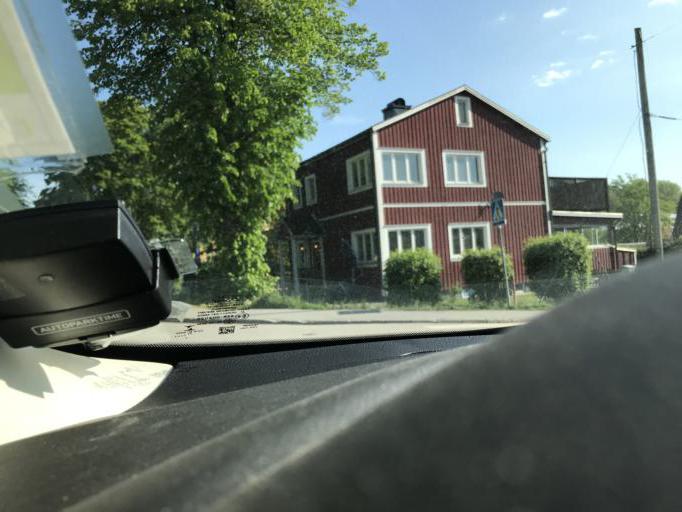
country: SE
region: Stockholm
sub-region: Botkyrka Kommun
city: Tumba
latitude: 59.1947
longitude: 17.8254
